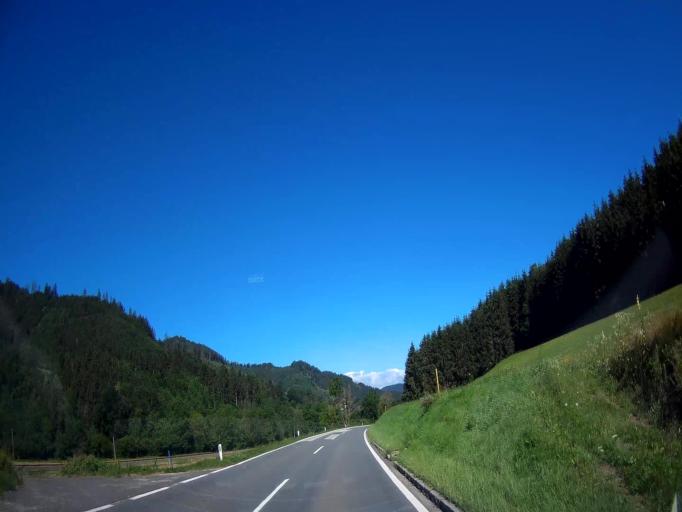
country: AT
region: Carinthia
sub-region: Politischer Bezirk Sankt Veit an der Glan
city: Bruckl
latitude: 46.7486
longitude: 14.5130
